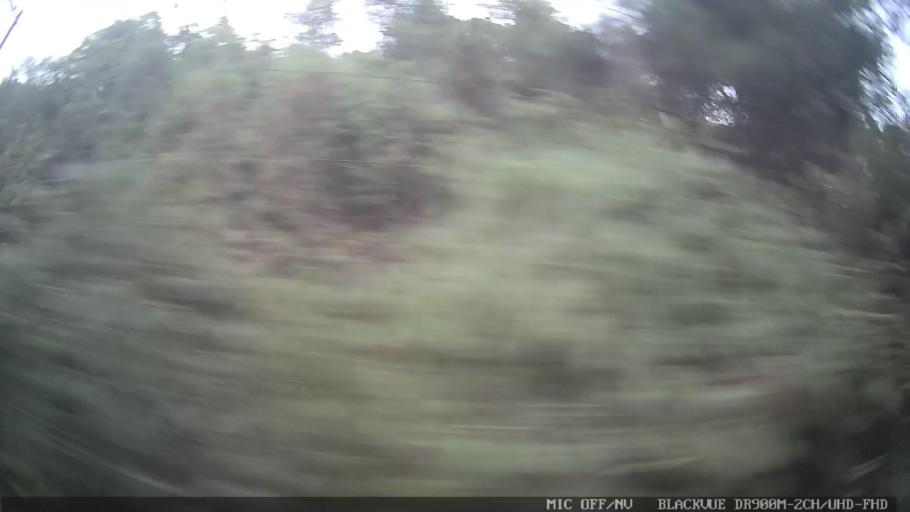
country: BR
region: Sao Paulo
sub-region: Rio Grande Da Serra
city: Rio Grande da Serra
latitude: -23.6970
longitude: -46.2884
